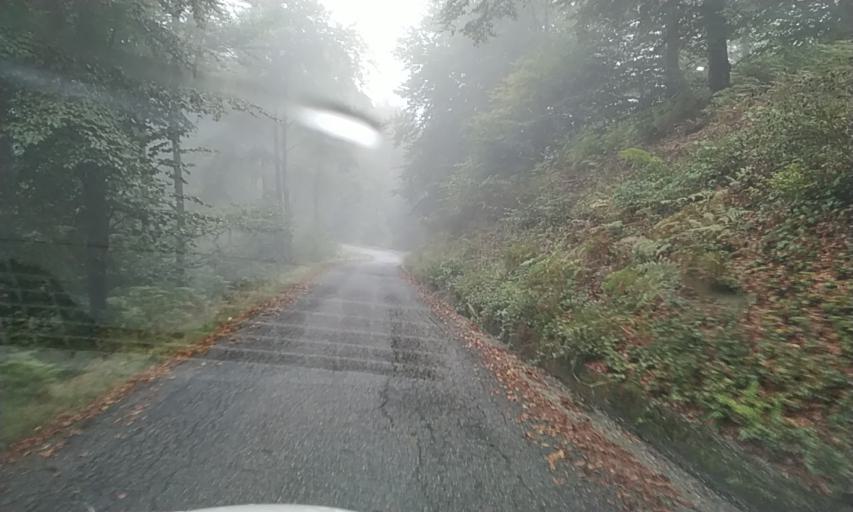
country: IT
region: Piedmont
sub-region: Provincia di Vercelli
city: Civiasco
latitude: 45.8351
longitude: 8.2945
